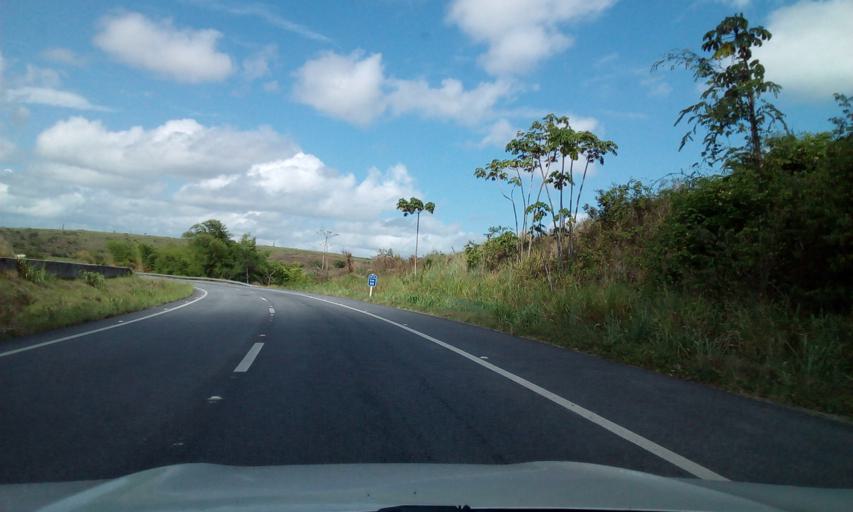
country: BR
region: Alagoas
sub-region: Rio Largo
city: Rio Largo
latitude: -9.4887
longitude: -35.8957
